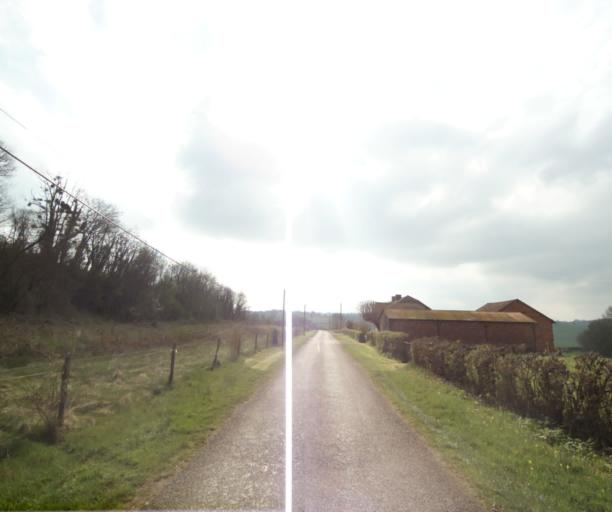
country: FR
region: Bourgogne
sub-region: Departement de Saone-et-Loire
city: Charolles
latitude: 46.4093
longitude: 4.2030
